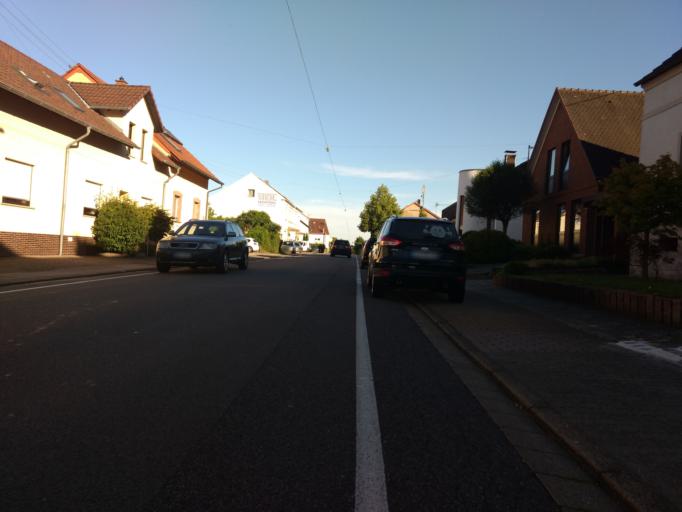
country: DE
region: Saarland
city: Rehlingen-Siersburg
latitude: 49.3794
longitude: 6.6772
